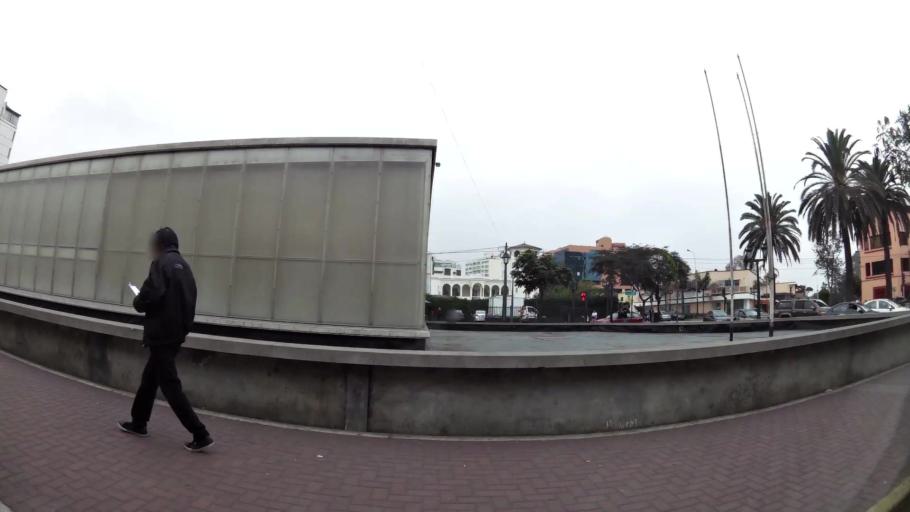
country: PE
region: Lima
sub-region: Lima
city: San Isidro
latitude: -12.0962
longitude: -77.0355
